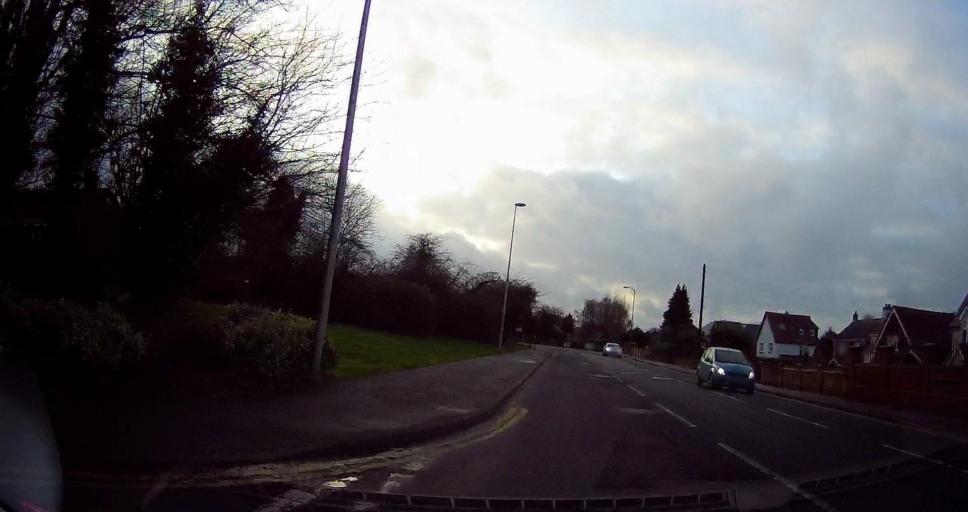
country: GB
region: England
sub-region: Kent
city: Chatham
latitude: 51.3592
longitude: 0.5134
